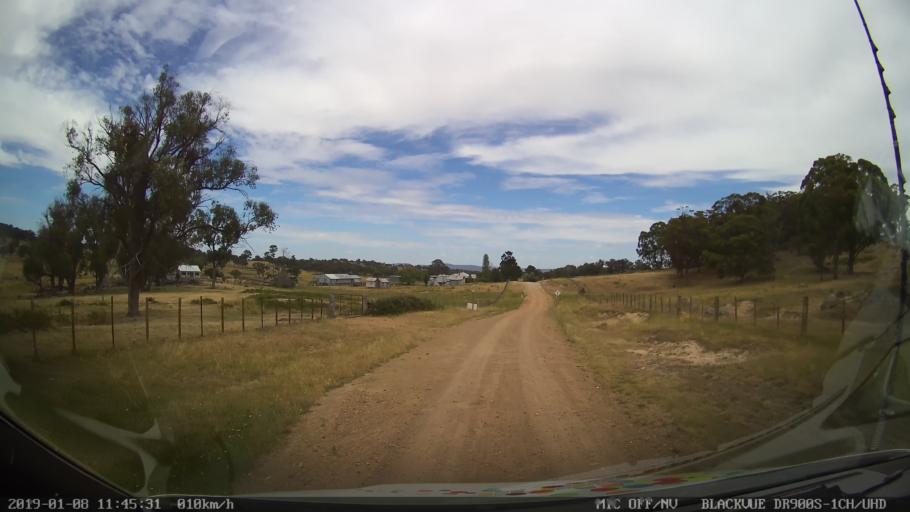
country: AU
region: New South Wales
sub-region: Armidale Dumaresq
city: Armidale
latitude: -30.3802
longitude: 151.5892
